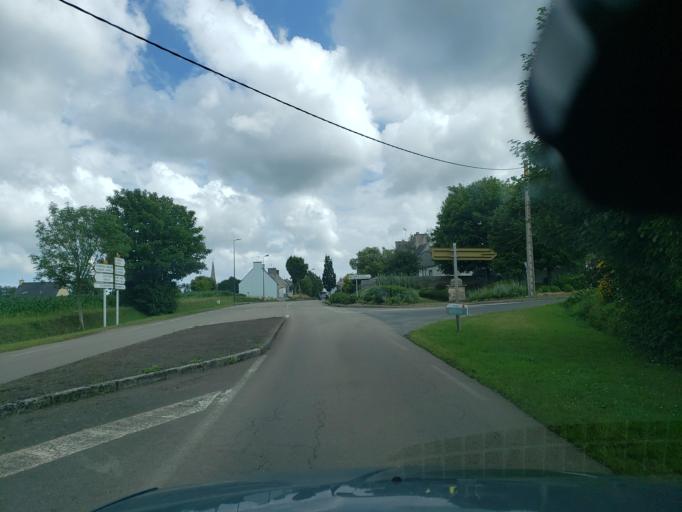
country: FR
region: Brittany
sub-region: Departement du Finistere
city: Ploneour-Lanvern
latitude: 47.8676
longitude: -4.2814
